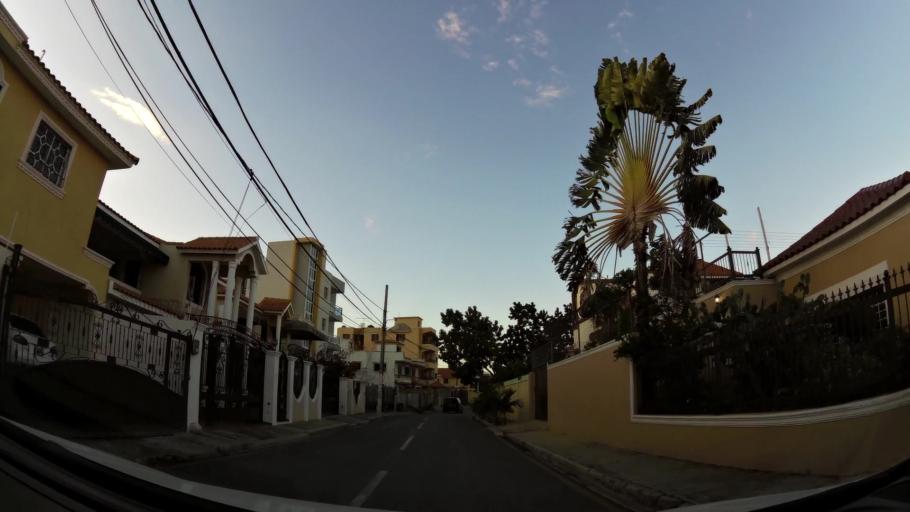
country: DO
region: Santo Domingo
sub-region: Santo Domingo
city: Santo Domingo Este
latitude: 18.4871
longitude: -69.8214
